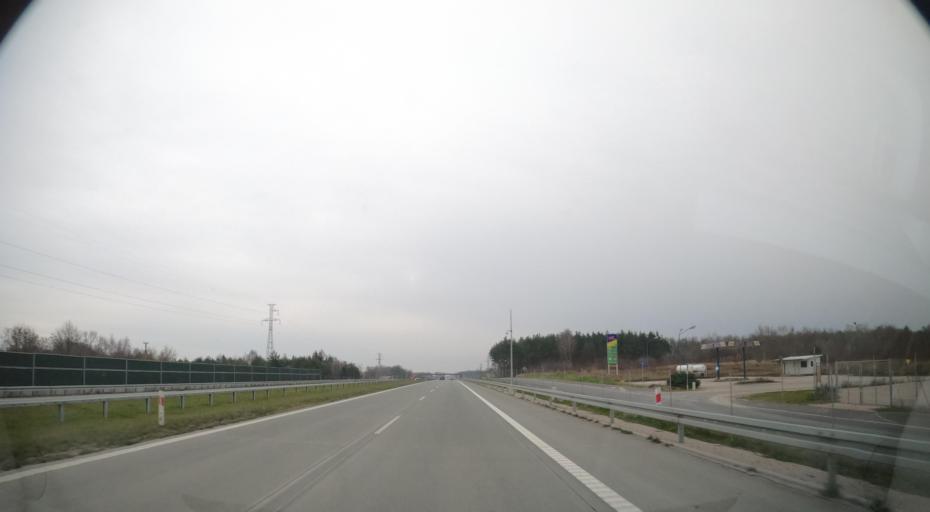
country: PL
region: Masovian Voivodeship
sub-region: Powiat piaseczynski
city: Tarczyn
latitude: 51.9235
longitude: 20.8515
